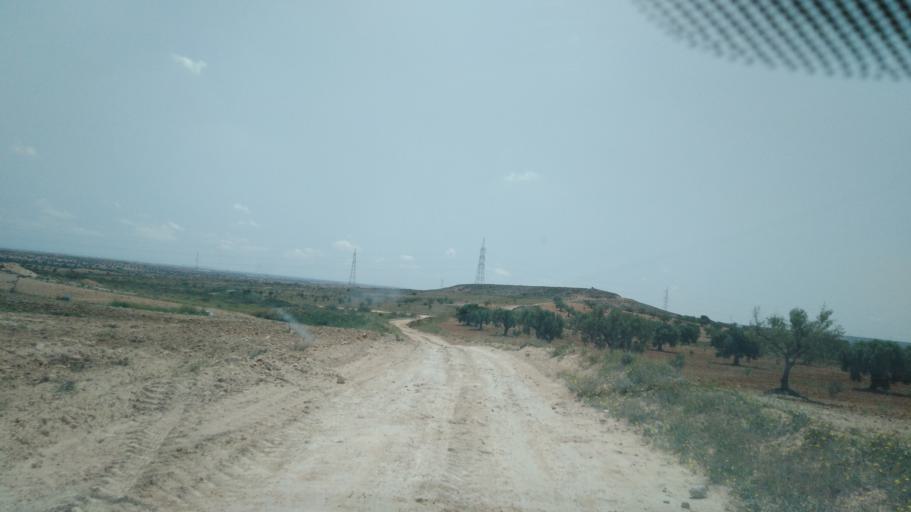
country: TN
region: Safaqis
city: Sfax
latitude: 34.7665
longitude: 10.5807
